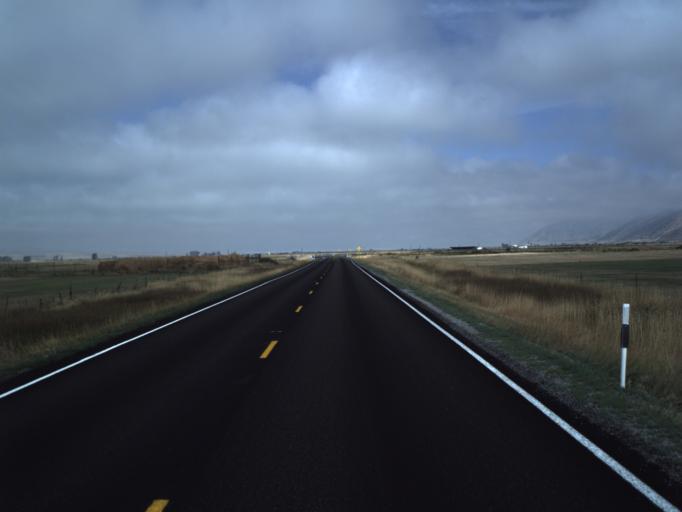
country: US
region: Utah
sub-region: Rich County
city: Randolph
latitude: 41.4991
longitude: -111.1224
